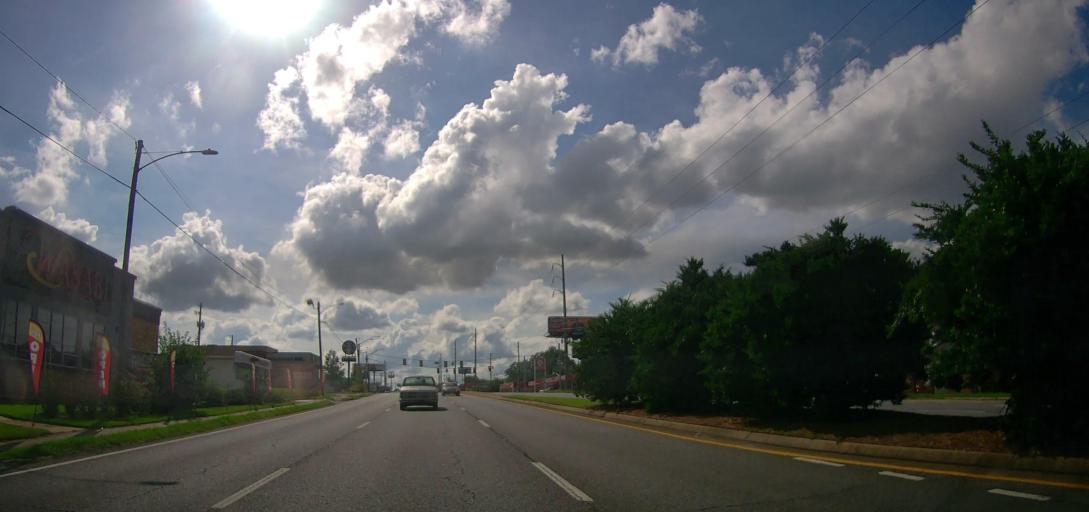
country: US
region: Alabama
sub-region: Russell County
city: Phenix City
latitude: 32.5071
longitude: -84.9650
